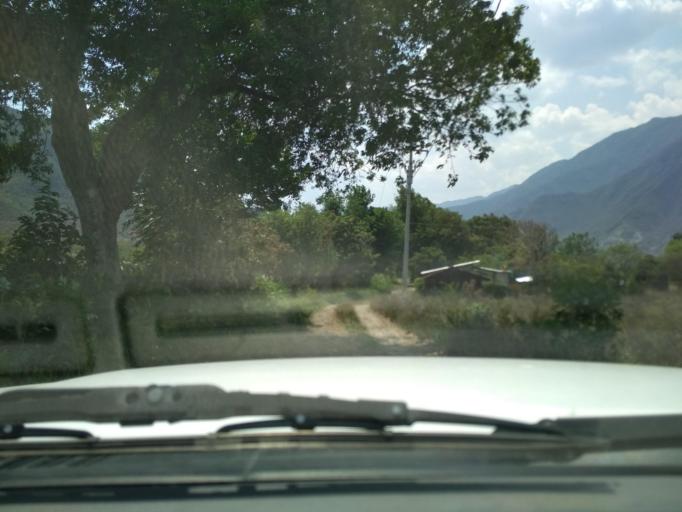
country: MX
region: Veracruz
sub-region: Acultzingo
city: Acatla
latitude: 18.7499
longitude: -97.2223
